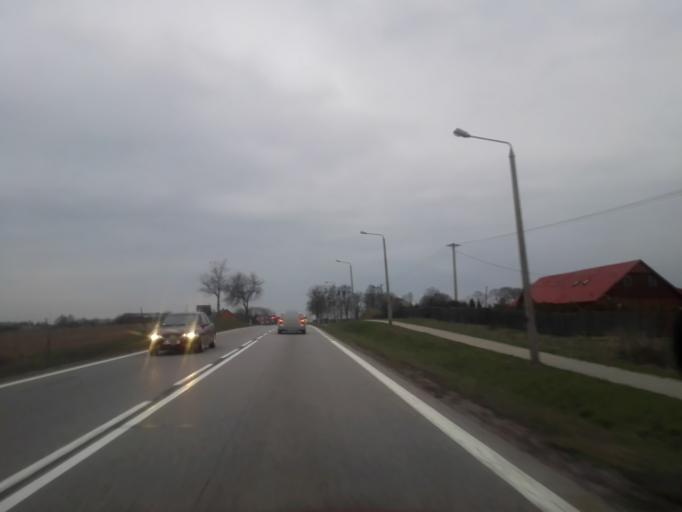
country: PL
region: Podlasie
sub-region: Powiat lomzynski
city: Piatnica
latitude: 53.2503
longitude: 22.1202
